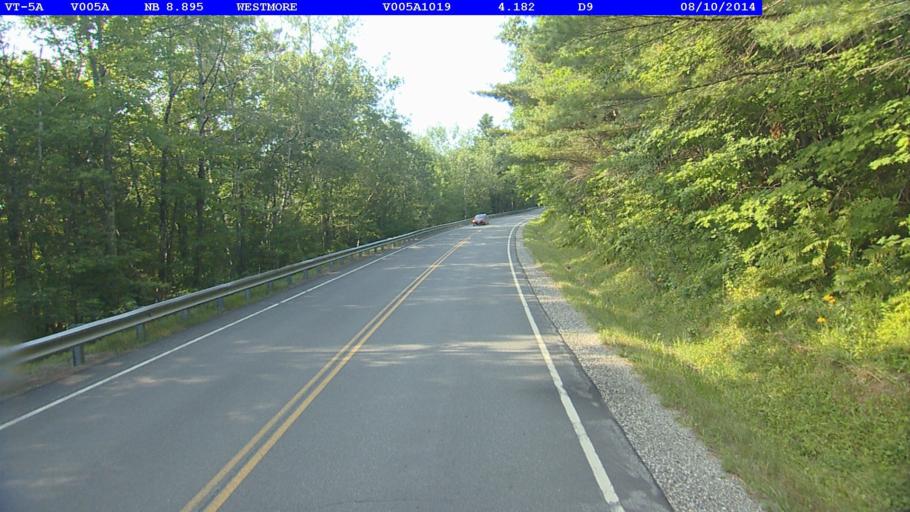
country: US
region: Vermont
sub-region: Caledonia County
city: Lyndonville
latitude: 44.7507
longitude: -72.0525
